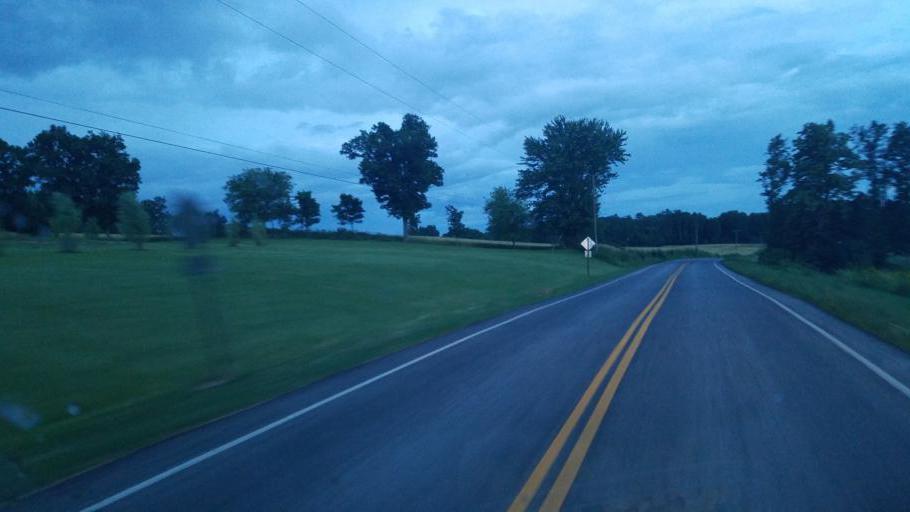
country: US
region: New York
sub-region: Wayne County
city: Clyde
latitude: 43.0313
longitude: -76.9091
